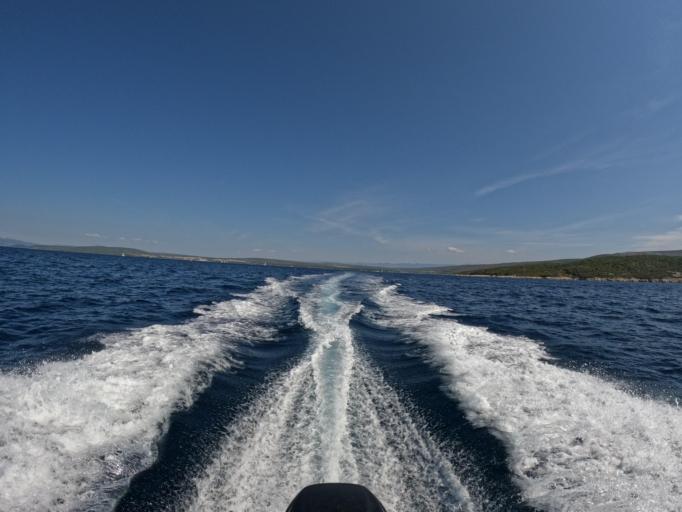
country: HR
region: Primorsko-Goranska
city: Punat
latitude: 44.9729
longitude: 14.6088
